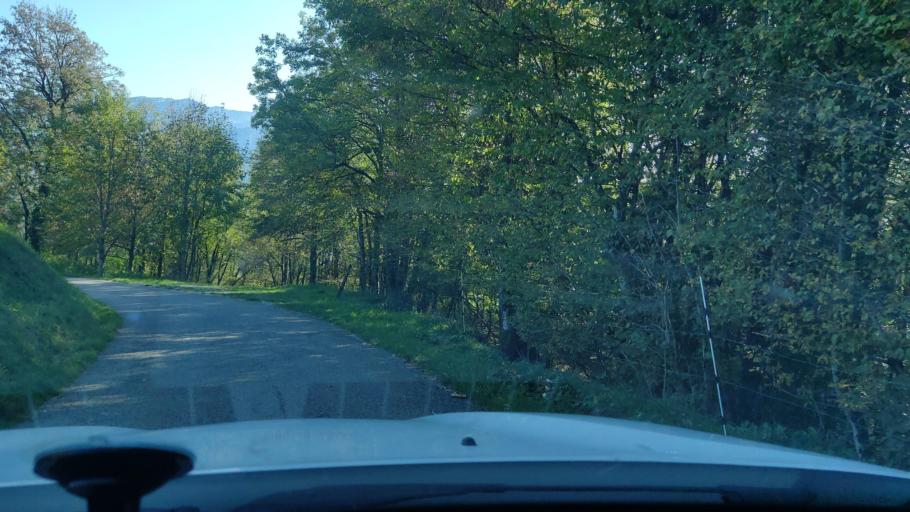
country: FR
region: Rhone-Alpes
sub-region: Departement de la Savoie
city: Les Echelles
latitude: 45.4653
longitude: 5.7800
